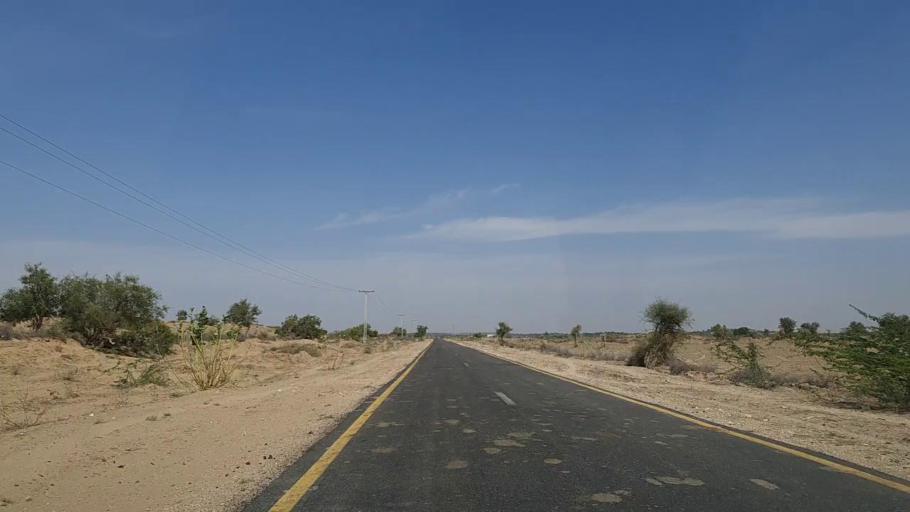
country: PK
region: Sindh
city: Mithi
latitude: 24.9578
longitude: 69.9067
